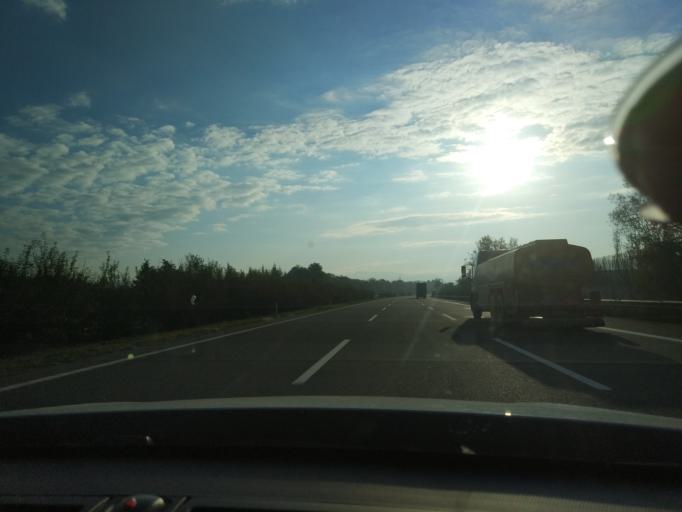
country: TR
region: Duzce
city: Duzce
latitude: 40.8040
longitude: 31.1673
